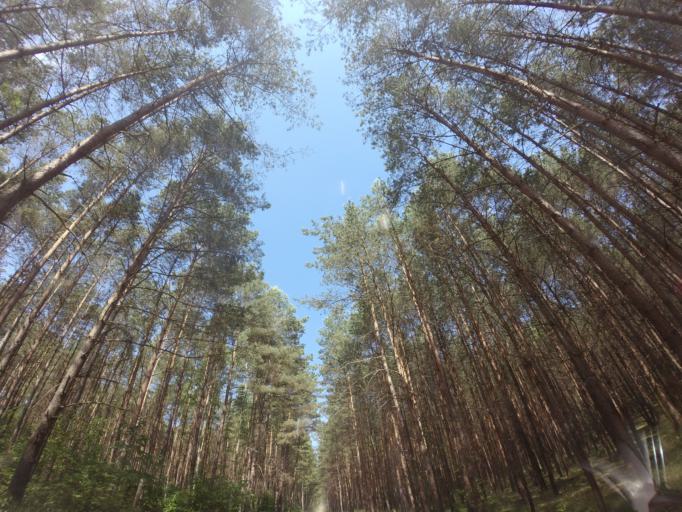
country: PL
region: West Pomeranian Voivodeship
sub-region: Powiat choszczenski
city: Drawno
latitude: 53.1231
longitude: 15.8535
